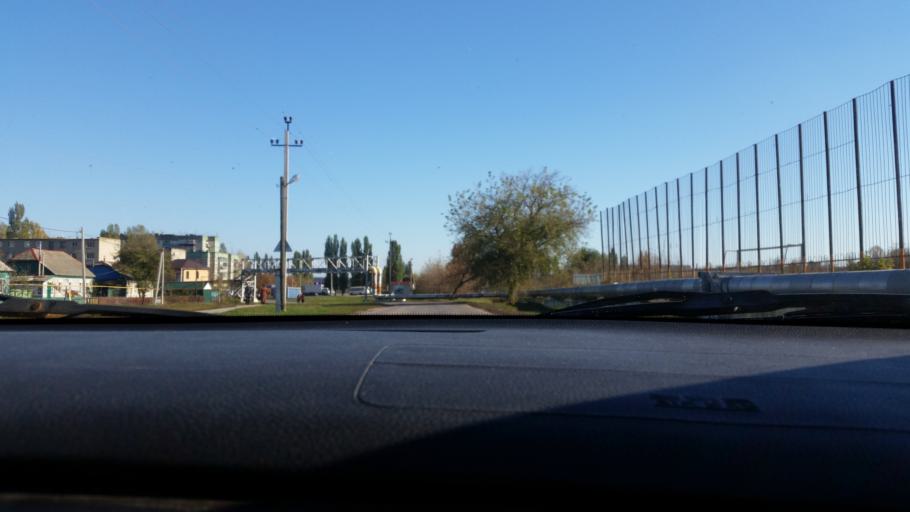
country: RU
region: Lipetsk
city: Gryazi
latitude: 52.4750
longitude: 39.9490
